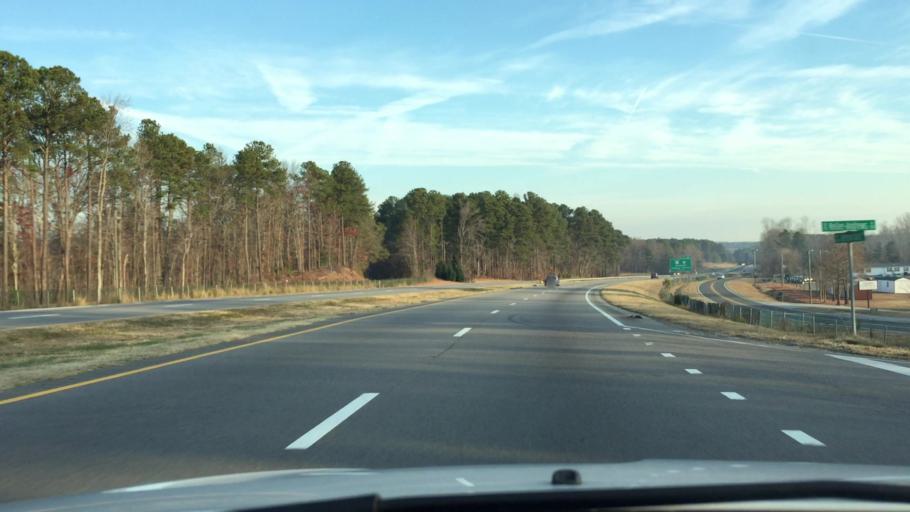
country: US
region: North Carolina
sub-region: Lee County
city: Sanford
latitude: 35.4509
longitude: -79.2142
